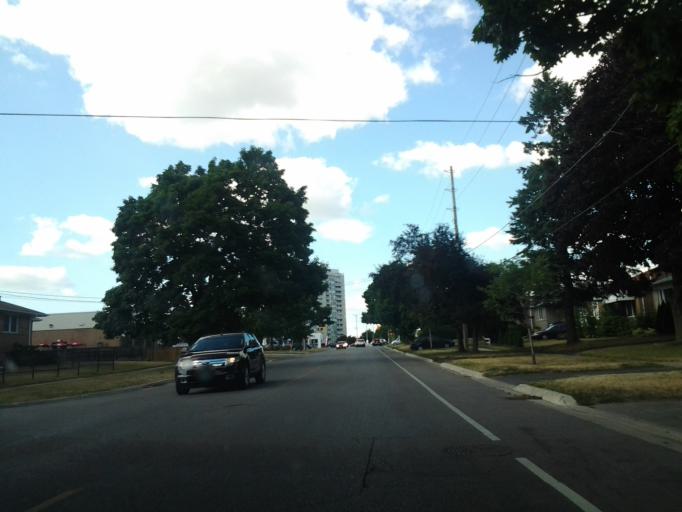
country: CA
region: Ontario
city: Brampton
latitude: 43.6473
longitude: -79.8809
